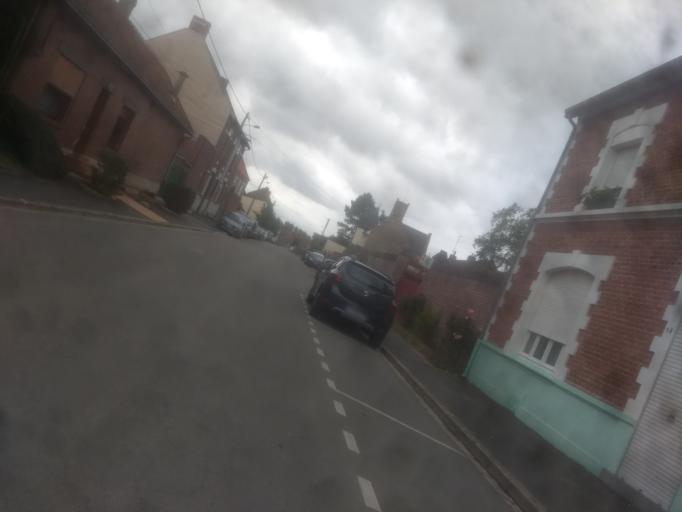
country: FR
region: Nord-Pas-de-Calais
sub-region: Departement du Pas-de-Calais
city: Saint-Nicolas
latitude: 50.3272
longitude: 2.7897
